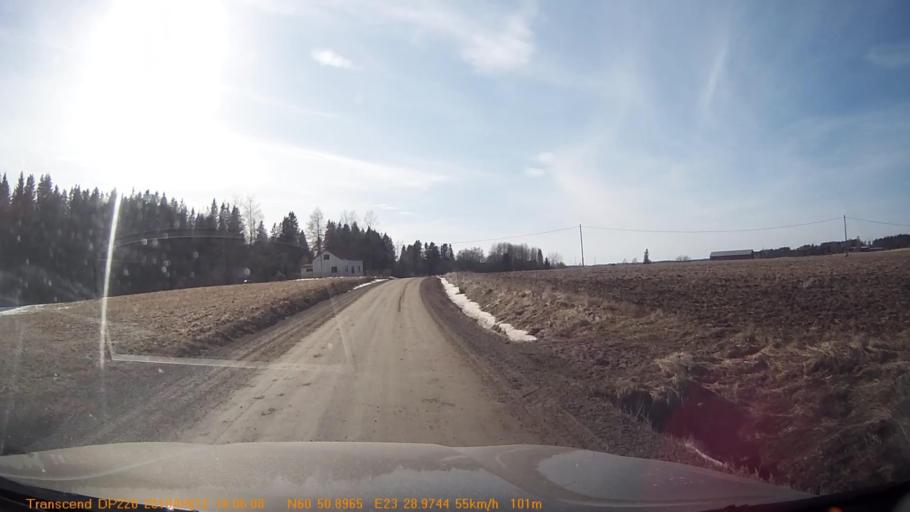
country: FI
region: Haeme
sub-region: Forssa
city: Jokioinen
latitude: 60.8483
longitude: 23.4826
